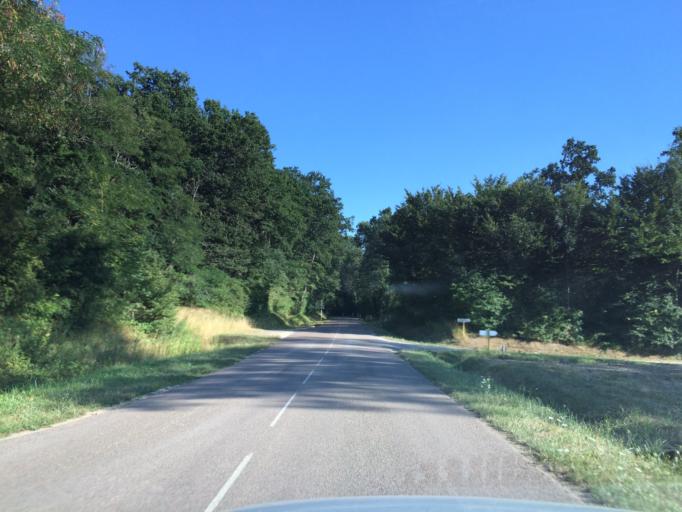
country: FR
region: Bourgogne
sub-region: Departement de l'Yonne
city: Fleury-la-Vallee
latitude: 47.8871
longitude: 3.4368
